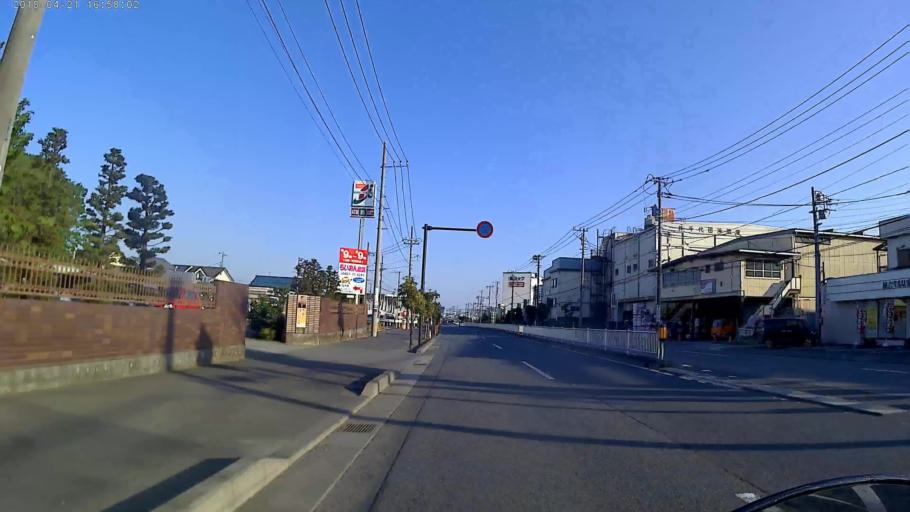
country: JP
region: Kanagawa
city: Minami-rinkan
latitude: 35.4523
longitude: 139.4183
